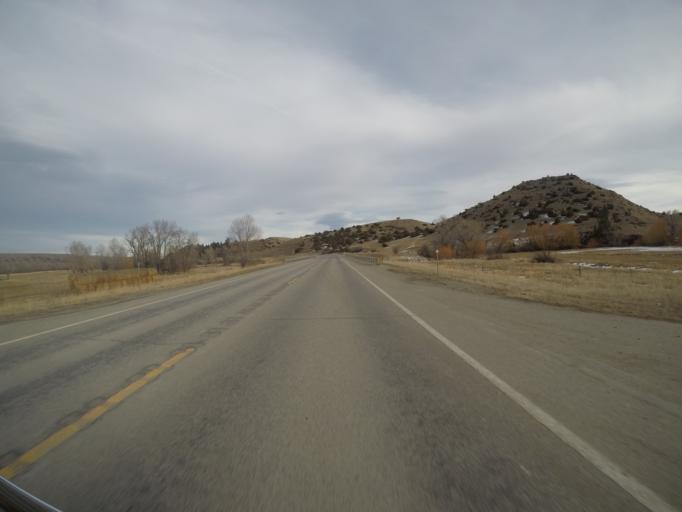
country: US
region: Montana
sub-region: Stillwater County
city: Absarokee
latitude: 45.5376
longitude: -109.4131
